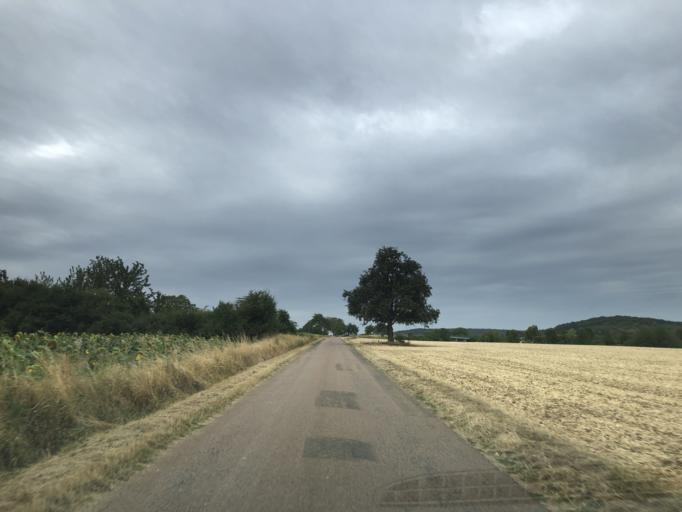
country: FR
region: Bourgogne
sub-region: Departement de l'Yonne
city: Aillant-sur-Tholon
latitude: 47.9096
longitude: 3.3433
